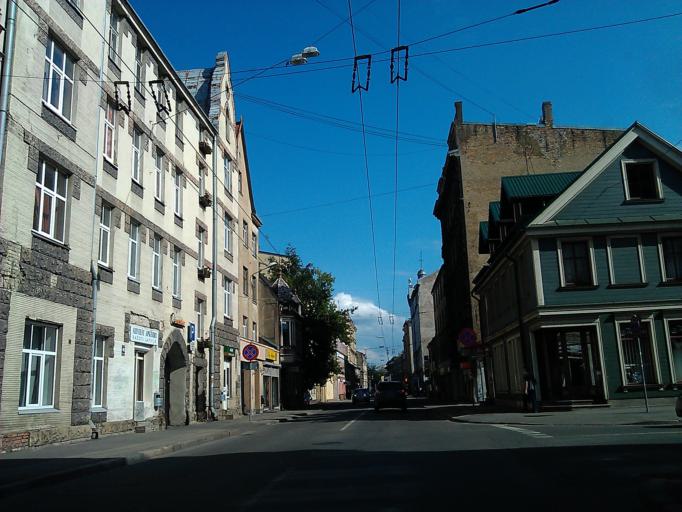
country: LV
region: Riga
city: Riga
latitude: 56.9620
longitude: 24.1387
